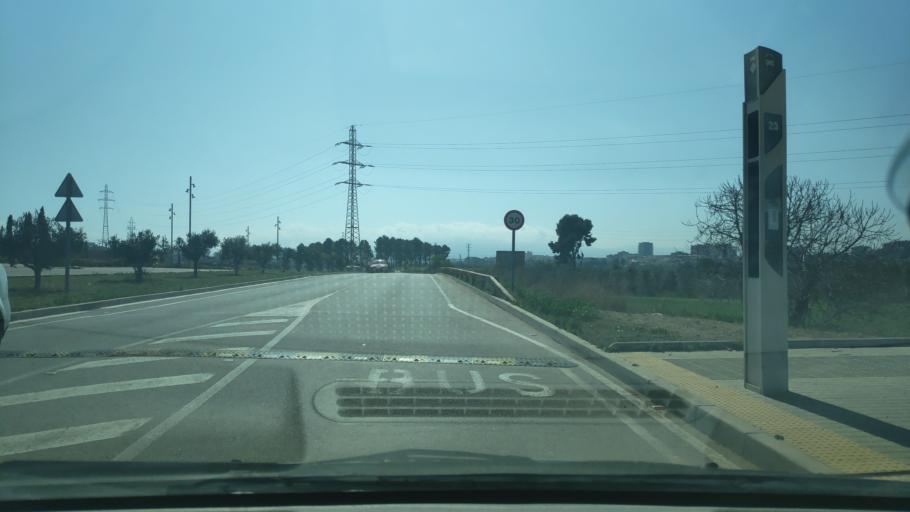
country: ES
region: Catalonia
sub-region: Provincia de Barcelona
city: Sabadell
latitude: 41.5578
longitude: 2.1210
